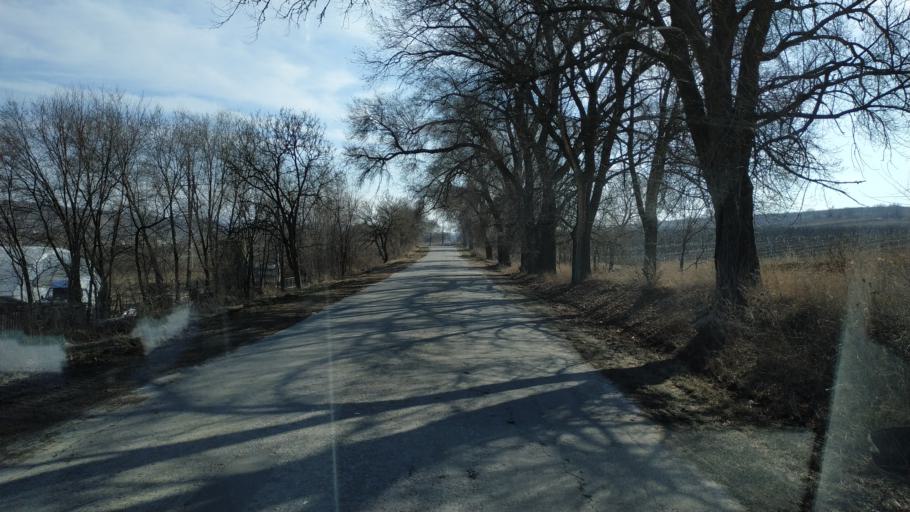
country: MD
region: Nisporeni
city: Nisporeni
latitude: 47.0809
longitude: 28.1443
